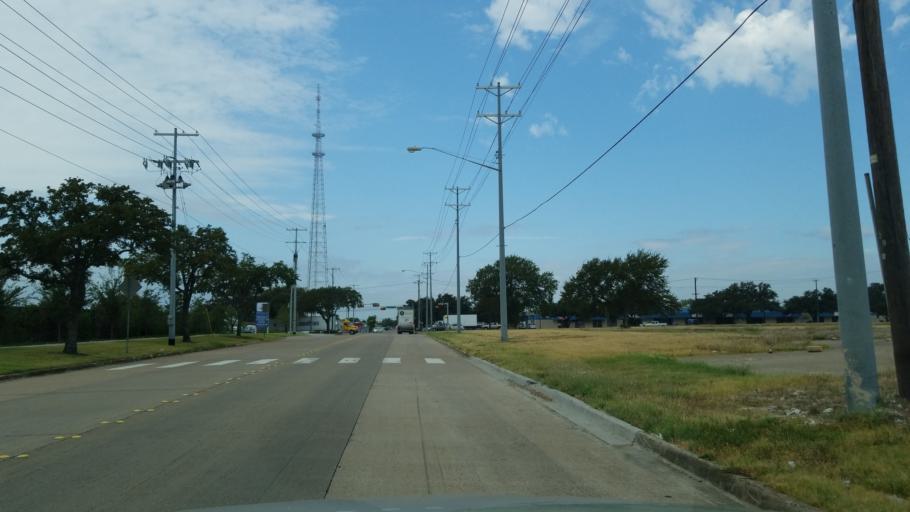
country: US
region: Texas
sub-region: Dallas County
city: Garland
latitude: 32.9018
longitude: -96.6812
